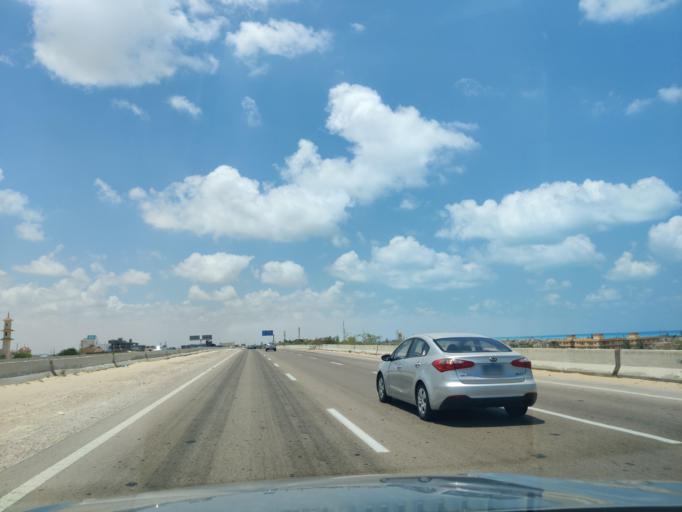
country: EG
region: Muhafazat Matruh
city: Al `Alamayn
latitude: 30.8233
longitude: 29.1819
